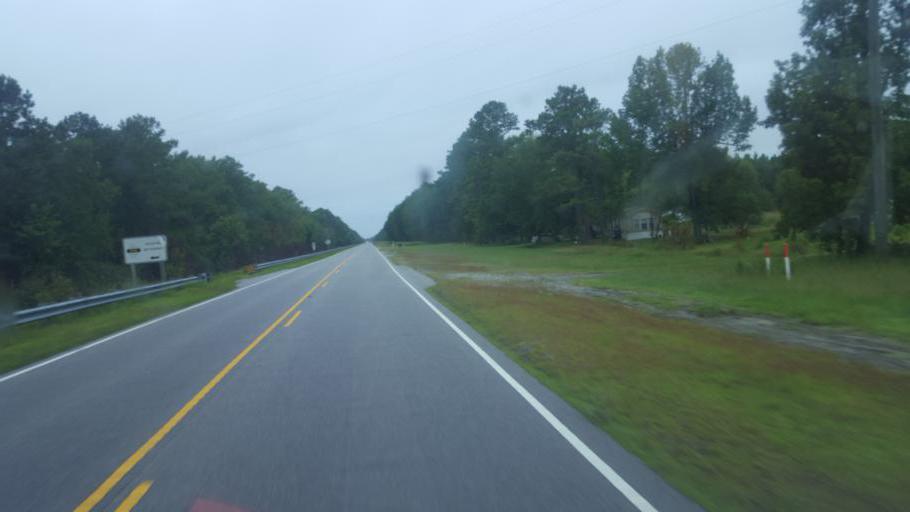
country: US
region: North Carolina
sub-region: Tyrrell County
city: Columbia
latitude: 35.9102
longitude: -76.1115
